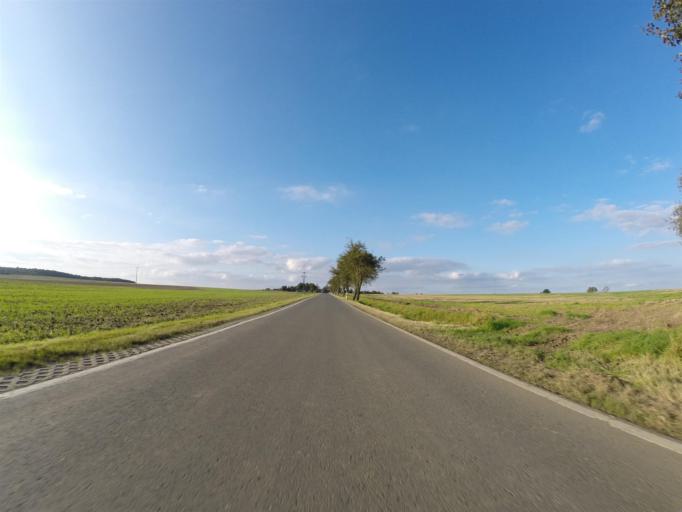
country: DE
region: Thuringia
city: Lehesten
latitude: 50.9672
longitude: 11.5391
